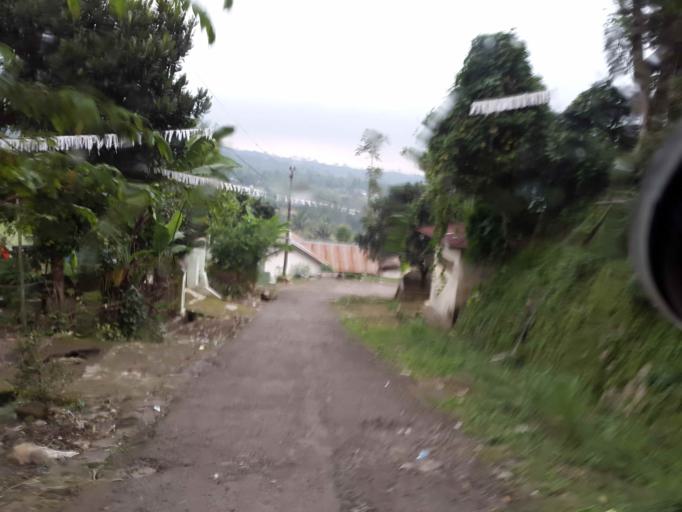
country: ID
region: Central Java
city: Lebaksiu
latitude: -7.1354
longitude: 109.1947
